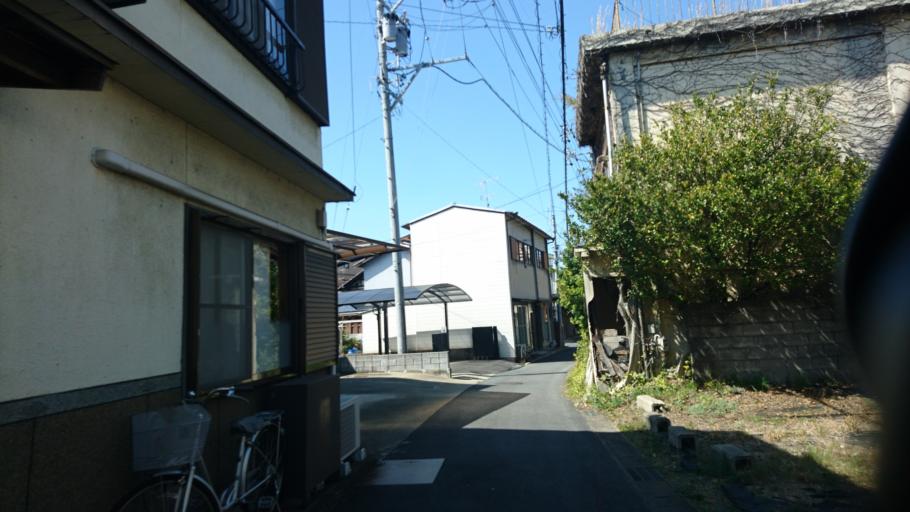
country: JP
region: Gifu
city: Nakatsugawa
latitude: 35.4534
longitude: 137.4106
